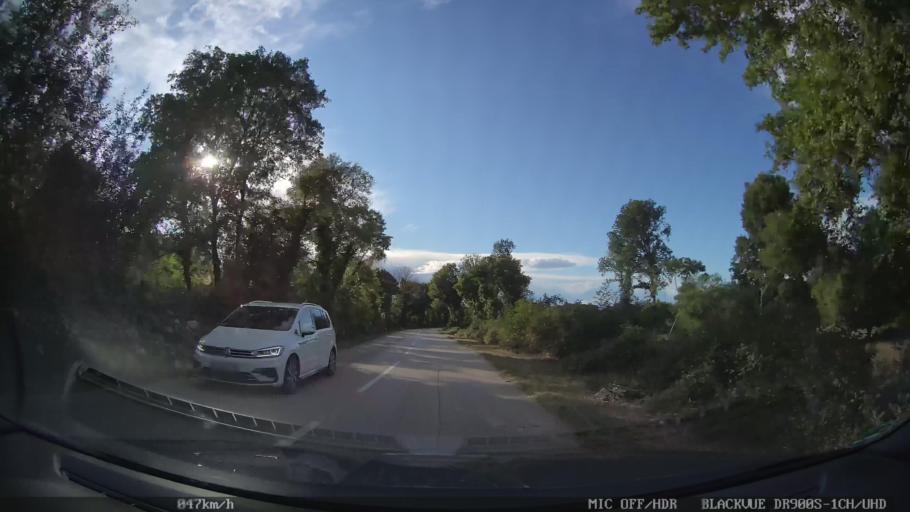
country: HR
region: Primorsko-Goranska
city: Njivice
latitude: 45.0979
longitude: 14.5334
